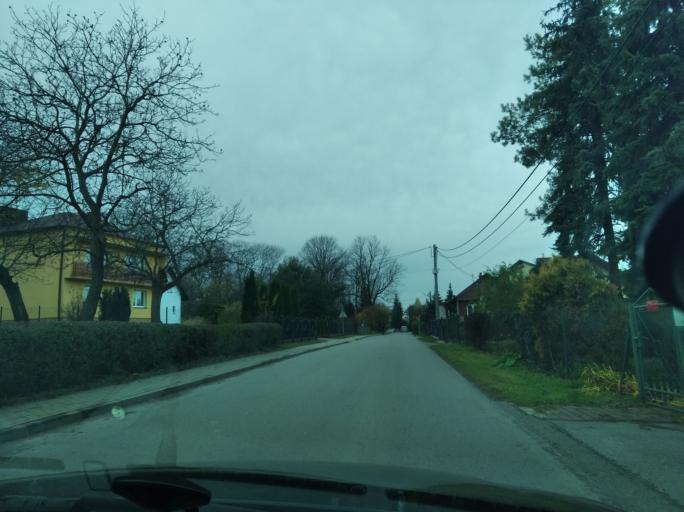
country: PL
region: Subcarpathian Voivodeship
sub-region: Powiat przeworski
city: Debow
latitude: 50.0452
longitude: 22.4335
